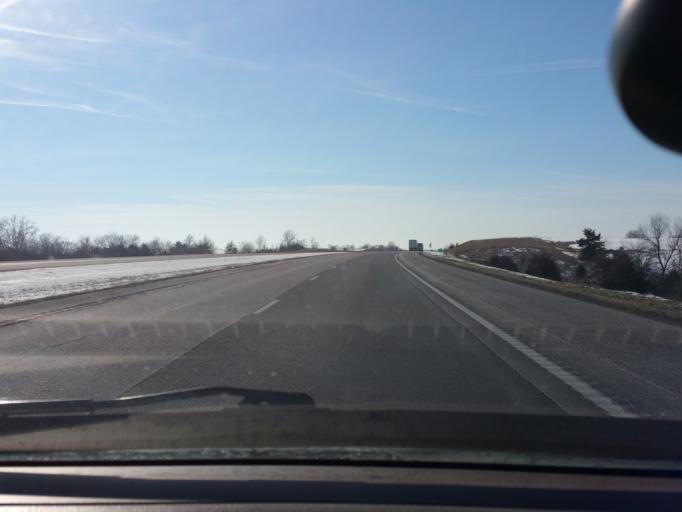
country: US
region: Missouri
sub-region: Harrison County
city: Bethany
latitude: 40.1778
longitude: -94.0166
